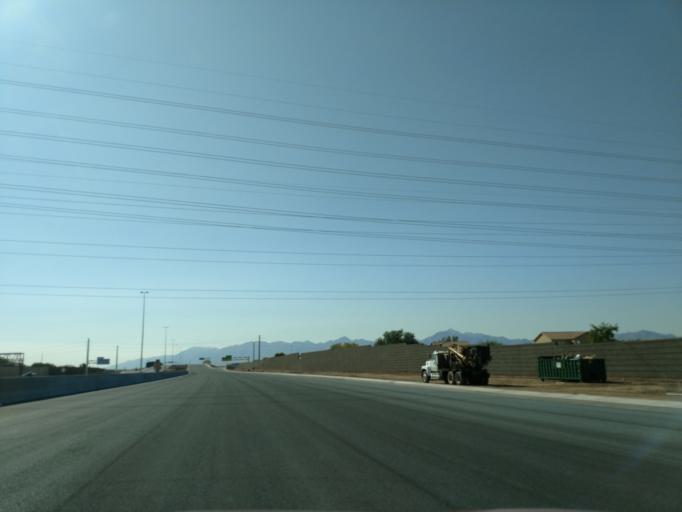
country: US
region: Arizona
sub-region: Maricopa County
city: Laveen
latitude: 33.4161
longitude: -112.1919
